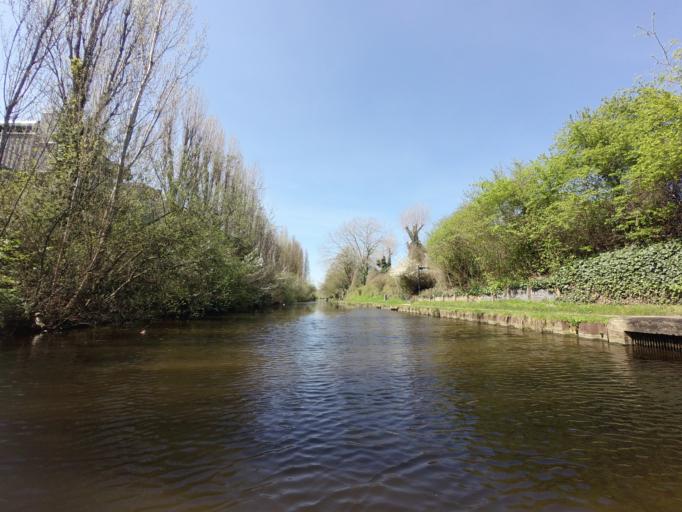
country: GB
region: England
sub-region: Greater London
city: Hayes
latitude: 51.5071
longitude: -0.4262
